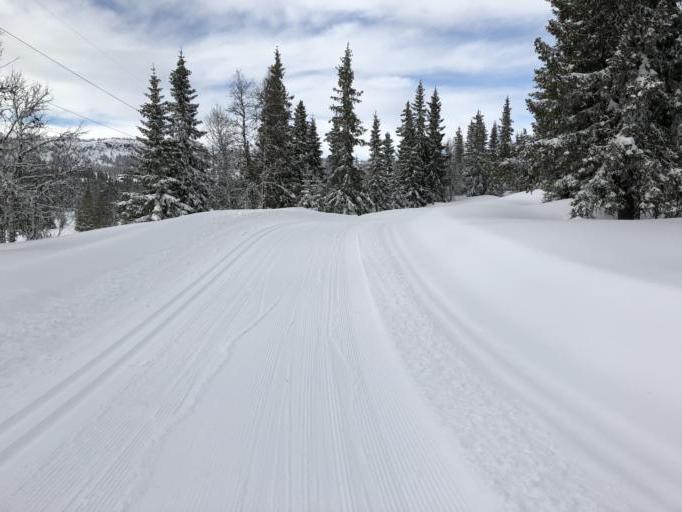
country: NO
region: Oppland
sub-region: Gausdal
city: Segalstad bru
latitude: 61.3236
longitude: 10.0787
